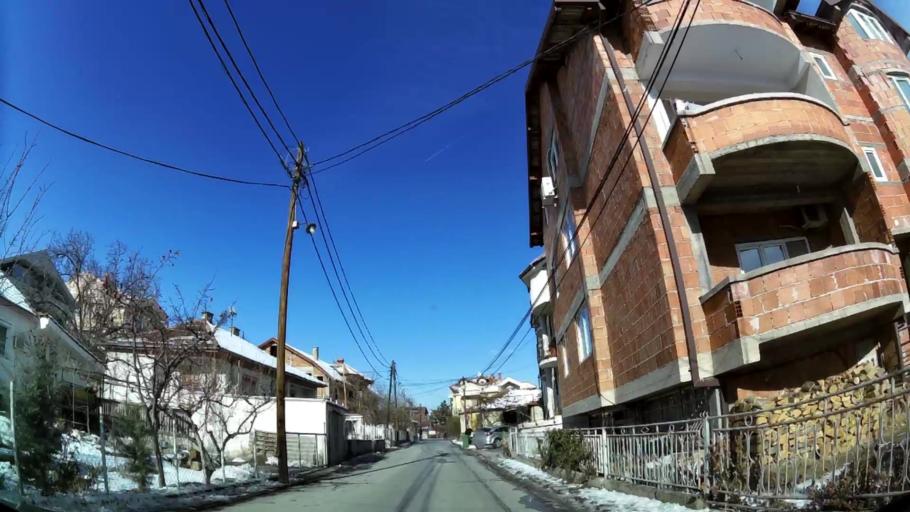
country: MK
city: Krushopek
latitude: 42.0083
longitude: 21.3578
